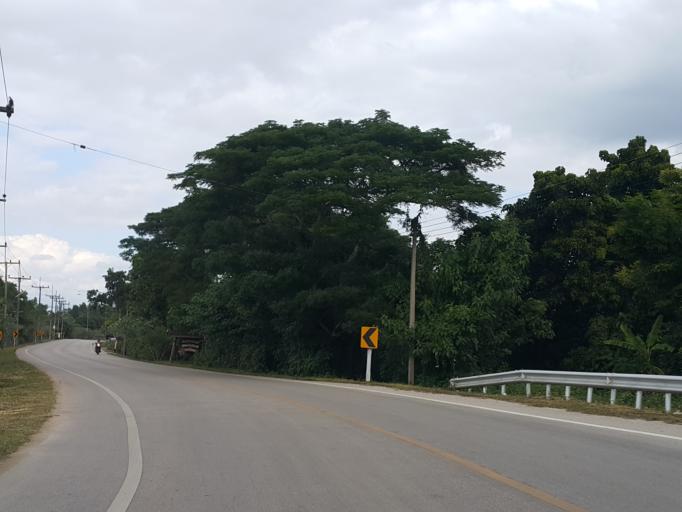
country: TH
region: Lampang
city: Chae Hom
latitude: 18.5793
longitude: 99.4714
